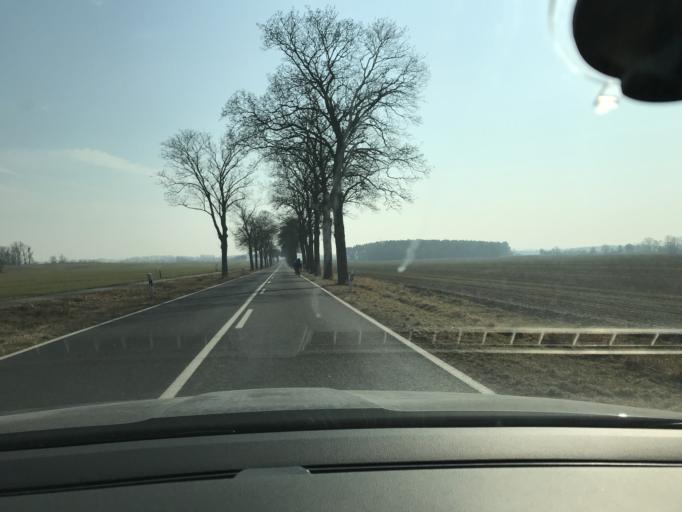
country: DE
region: Brandenburg
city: Mittenwalde
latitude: 52.2928
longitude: 13.5211
